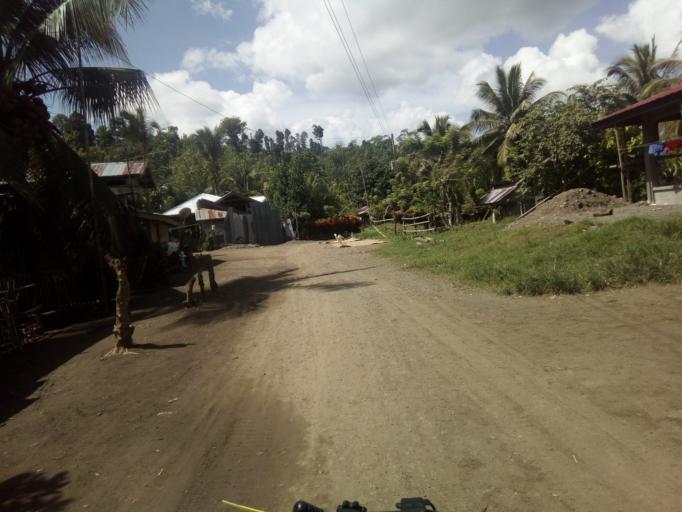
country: PH
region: Caraga
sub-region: Province of Agusan del Sur
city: Santa Josefa
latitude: 7.9794
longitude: 125.9757
